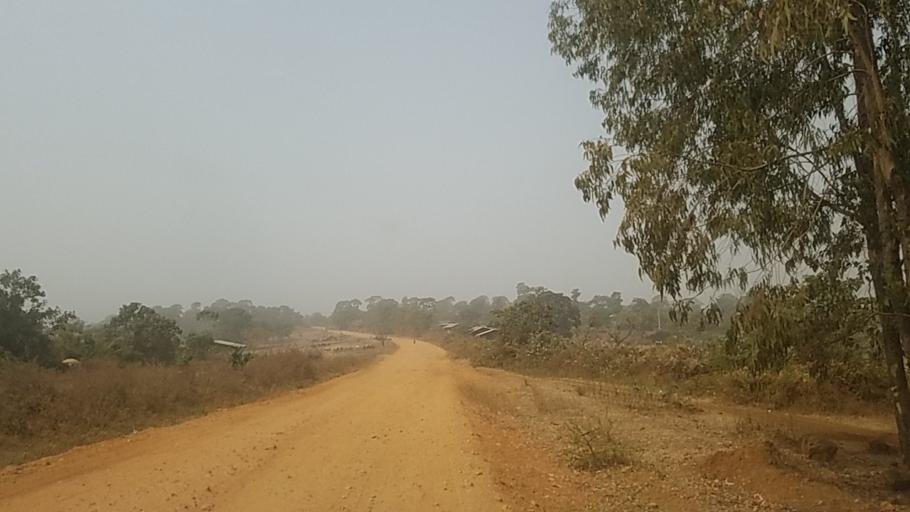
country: ET
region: Amhara
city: Bure
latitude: 10.7967
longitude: 36.3214
